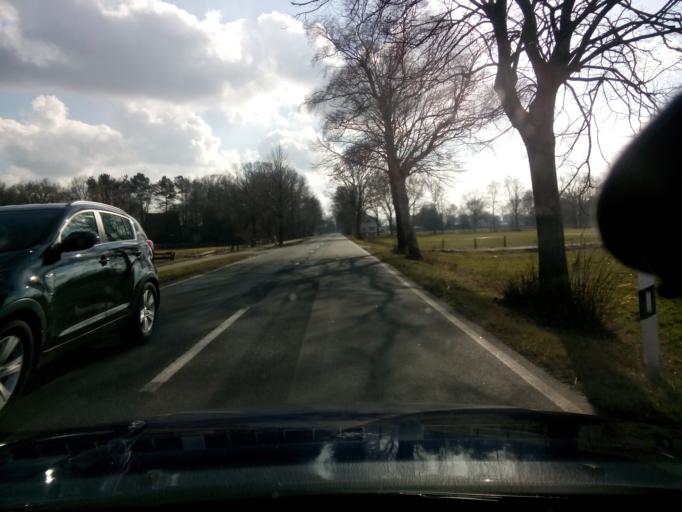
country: DE
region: Lower Saxony
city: Vollersode
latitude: 53.3229
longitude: 8.9794
